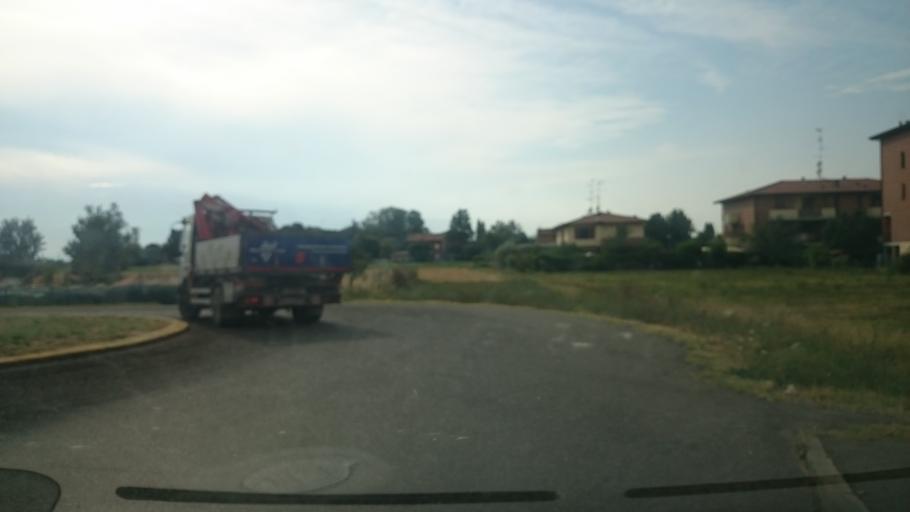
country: IT
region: Emilia-Romagna
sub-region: Provincia di Reggio Emilia
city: Reggio nell'Emilia
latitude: 44.6723
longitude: 10.5990
